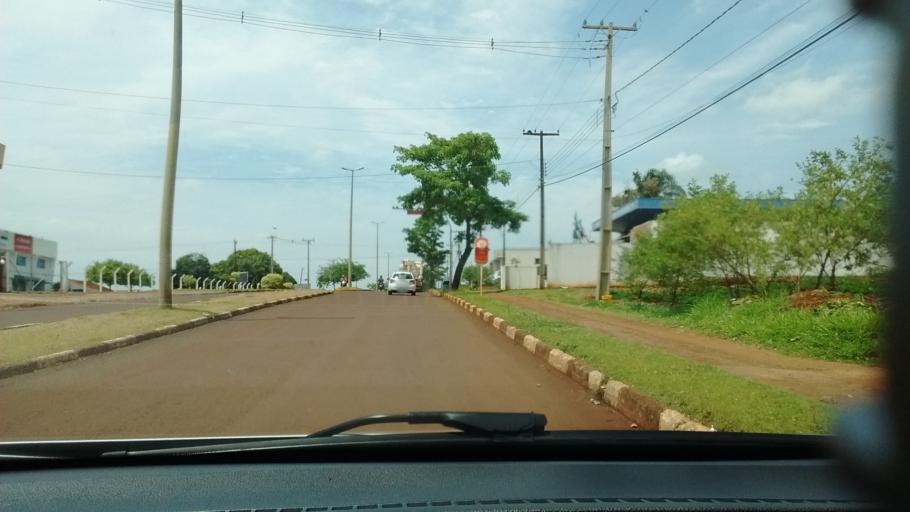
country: BR
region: Parana
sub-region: Corbelia
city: Corbelia
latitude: -24.5536
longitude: -52.9953
